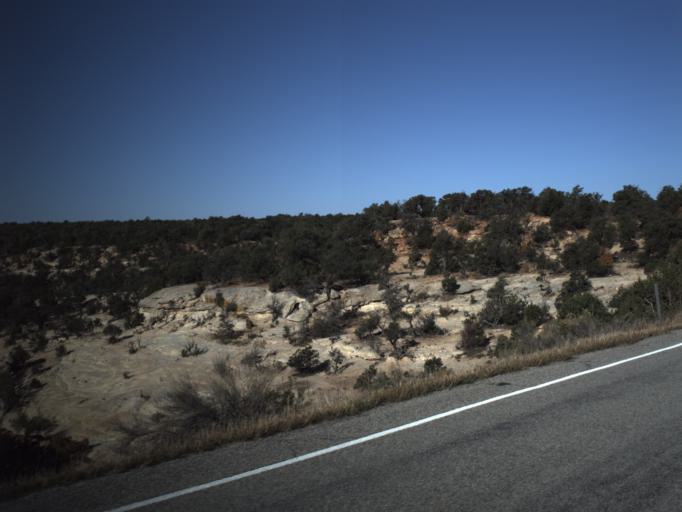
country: US
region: Utah
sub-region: San Juan County
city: Blanding
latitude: 37.5838
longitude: -109.8922
